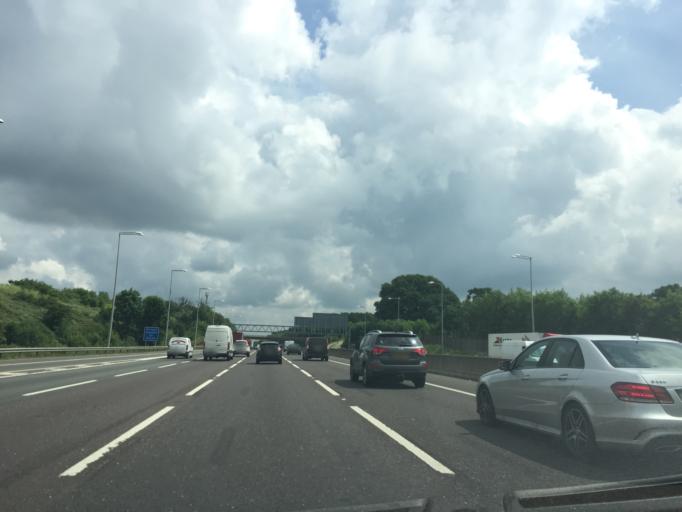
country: GB
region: England
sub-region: Hertfordshire
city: St Albans
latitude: 51.7134
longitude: -0.3656
